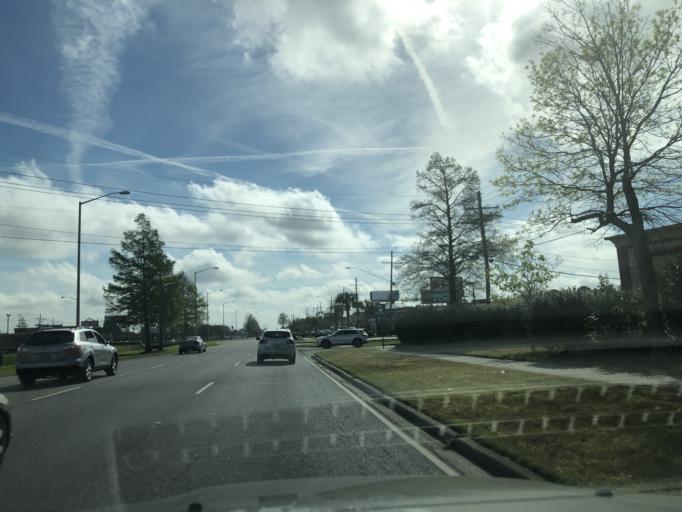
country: US
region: Louisiana
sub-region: Jefferson Parish
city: Kenner
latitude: 30.0059
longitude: -90.2005
